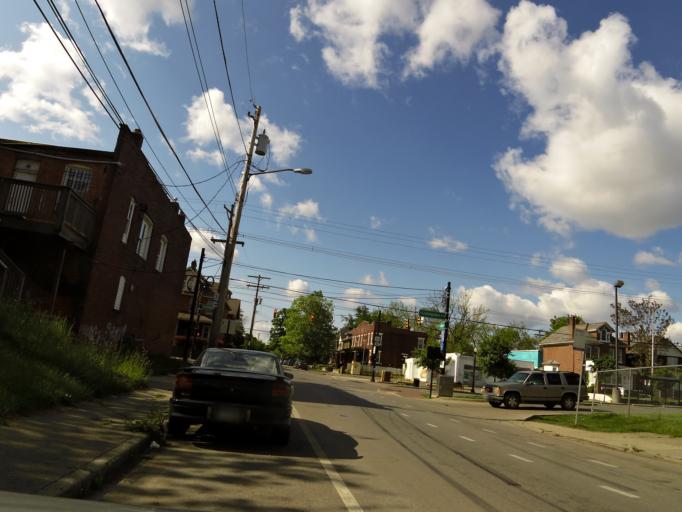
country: US
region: Ohio
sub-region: Franklin County
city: Columbus
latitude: 39.9501
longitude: -82.9714
